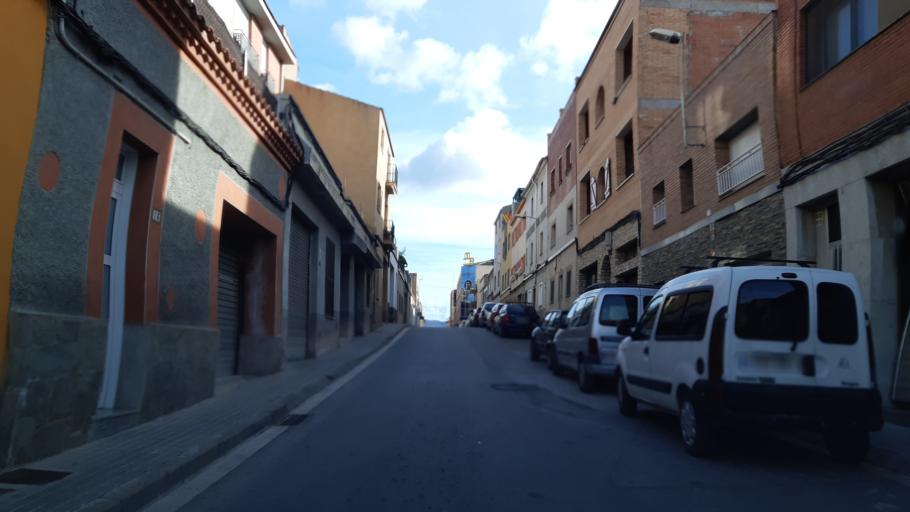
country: ES
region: Catalonia
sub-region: Provincia de Barcelona
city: Vilanova del Cami
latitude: 41.5708
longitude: 1.6366
